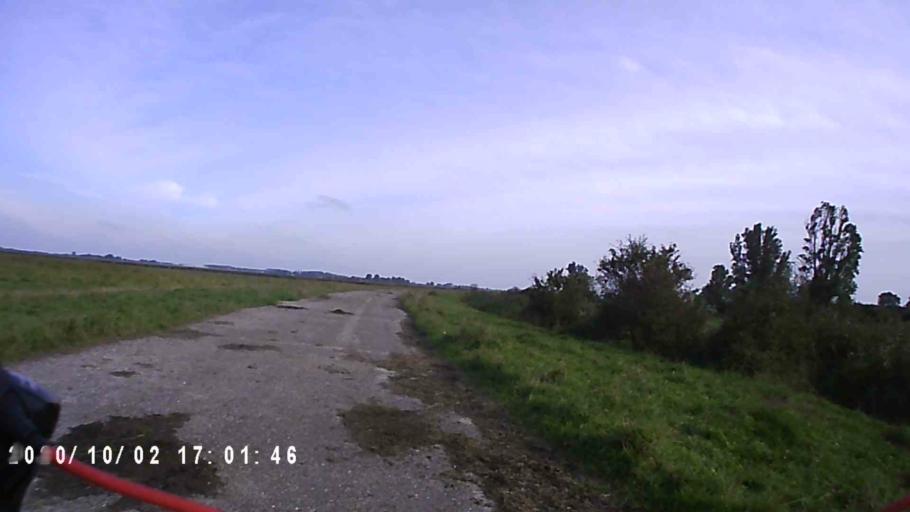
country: NL
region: Groningen
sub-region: Gemeente De Marne
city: Ulrum
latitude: 53.3431
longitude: 6.2611
